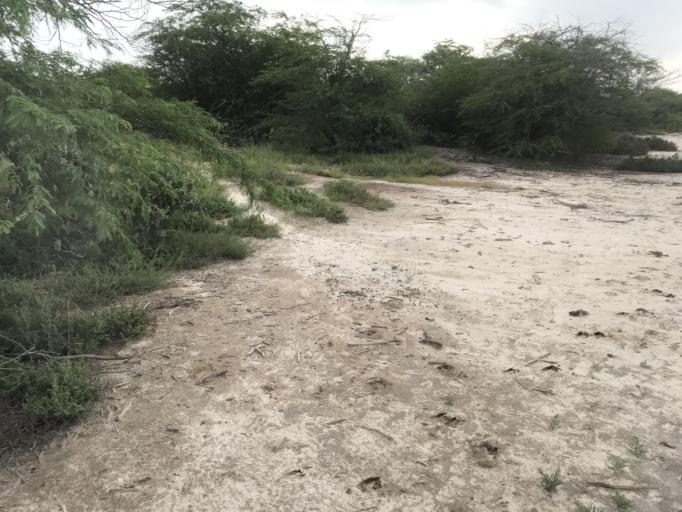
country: SN
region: Saint-Louis
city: Saint-Louis
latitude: 15.9272
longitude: -16.4670
